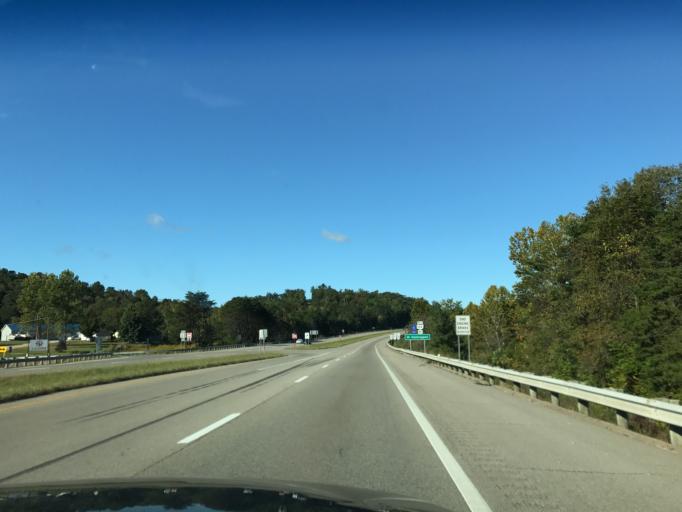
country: US
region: West Virginia
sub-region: Wood County
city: Washington
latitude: 39.2378
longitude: -81.7436
